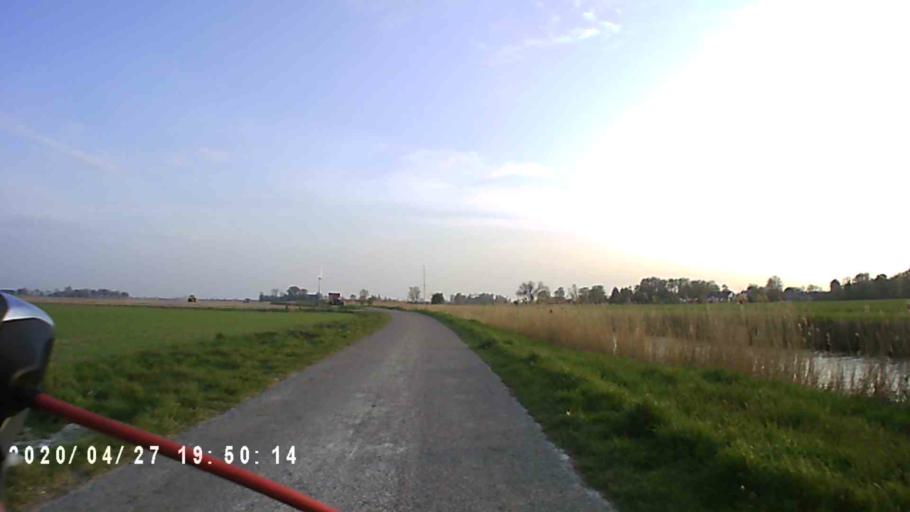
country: NL
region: Groningen
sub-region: Gemeente Zuidhorn
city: Oldehove
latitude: 53.3421
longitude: 6.4315
